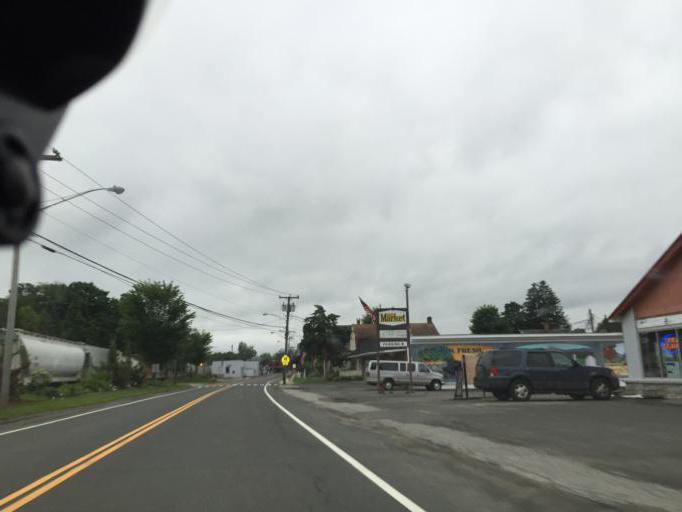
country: US
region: Connecticut
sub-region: Litchfield County
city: Canaan
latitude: 42.0301
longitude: -73.3281
